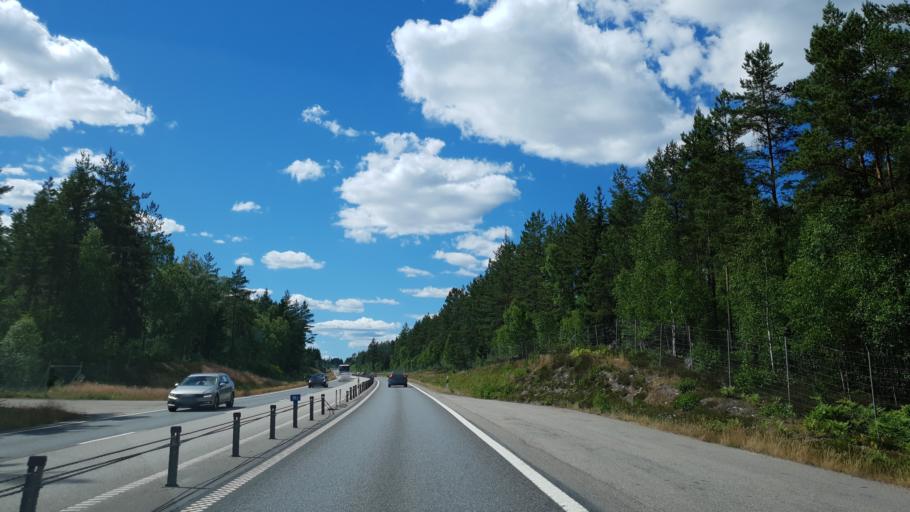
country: SE
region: Kronoberg
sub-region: Vaxjo Kommun
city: Vaexjoe
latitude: 56.8751
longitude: 14.9287
